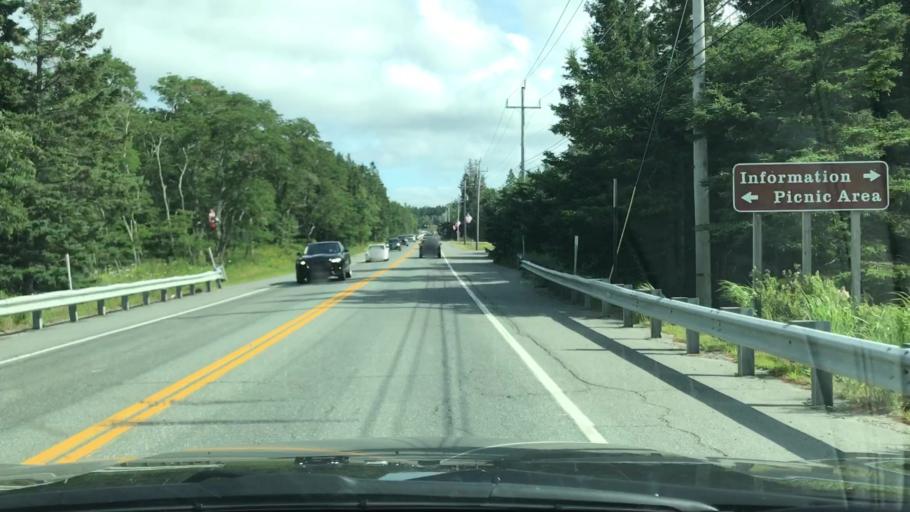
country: US
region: Maine
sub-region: Hancock County
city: Trenton
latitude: 44.4284
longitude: -68.3668
